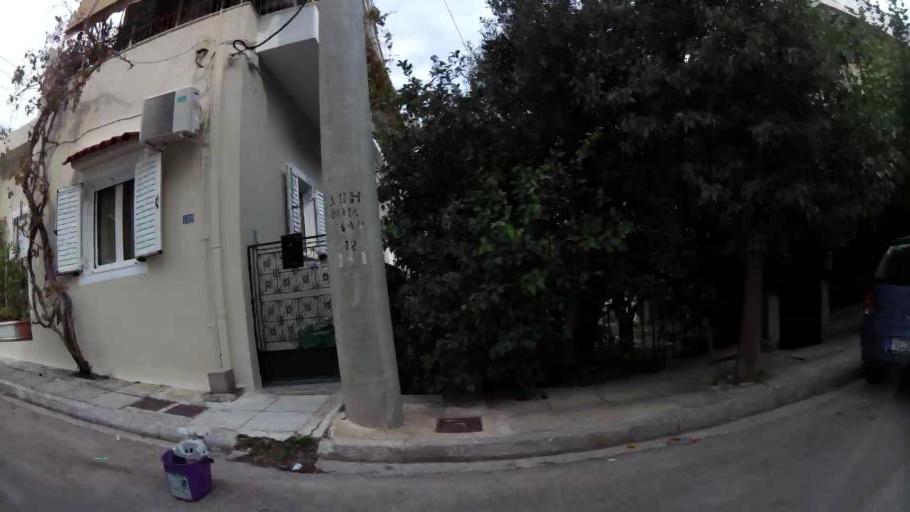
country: GR
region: Attica
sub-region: Nomarchia Athinas
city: Chaidari
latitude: 38.0197
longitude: 23.6500
